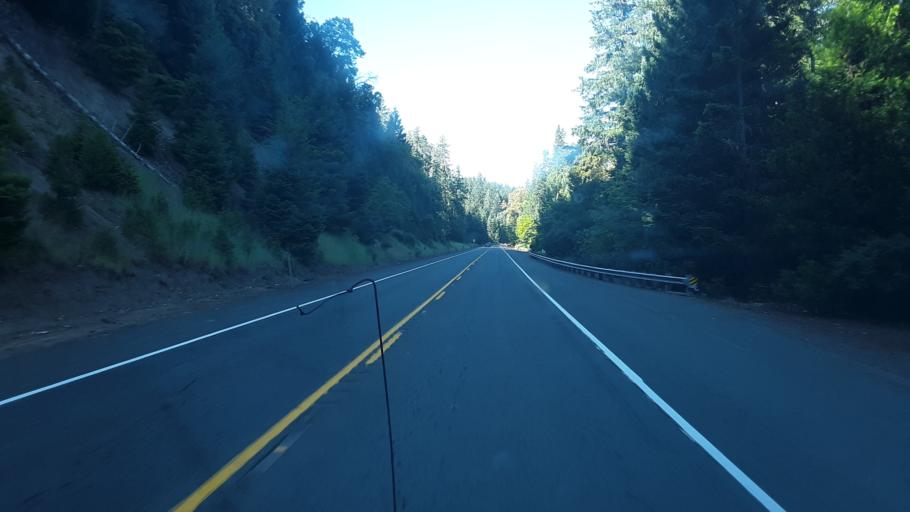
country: US
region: Oregon
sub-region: Jackson County
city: Shady Cove
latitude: 42.6795
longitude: -122.6173
